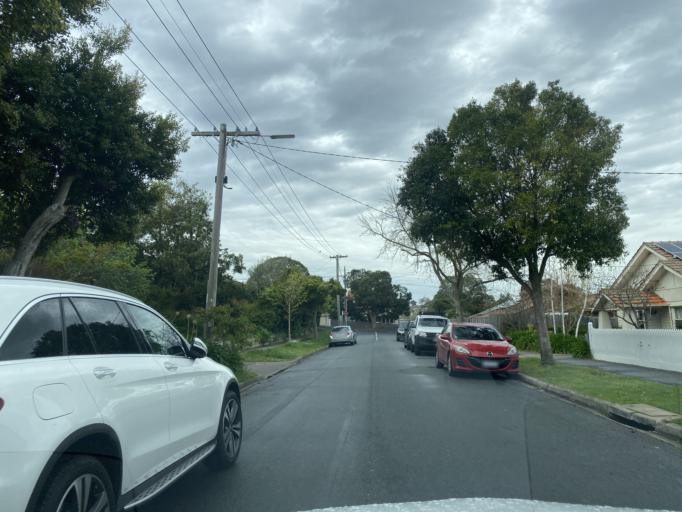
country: AU
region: Victoria
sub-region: Boroondara
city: Camberwell
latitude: -37.8451
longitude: 145.0790
